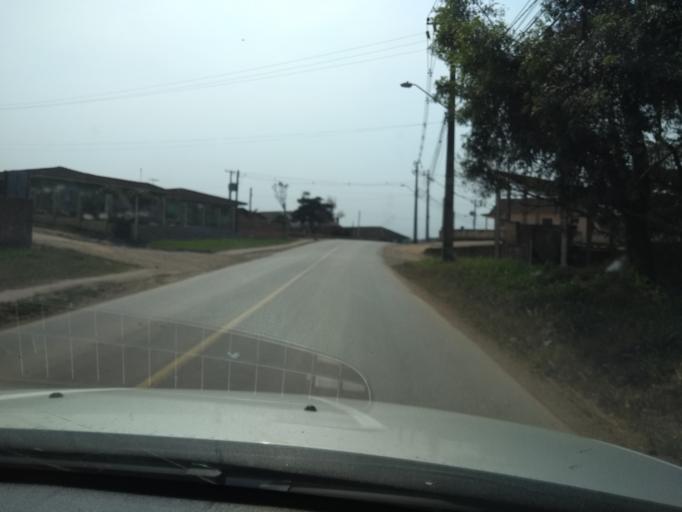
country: BR
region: Parana
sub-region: Araucaria
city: Araucaria
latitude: -25.6063
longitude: -49.3305
